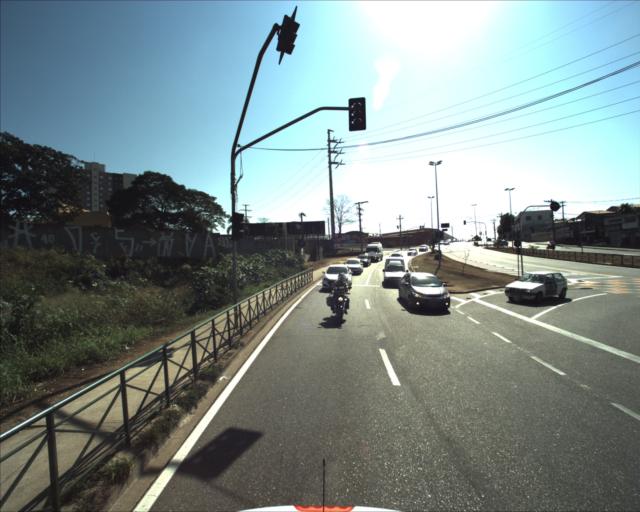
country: BR
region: Sao Paulo
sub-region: Sorocaba
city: Sorocaba
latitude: -23.4552
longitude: -47.4828
